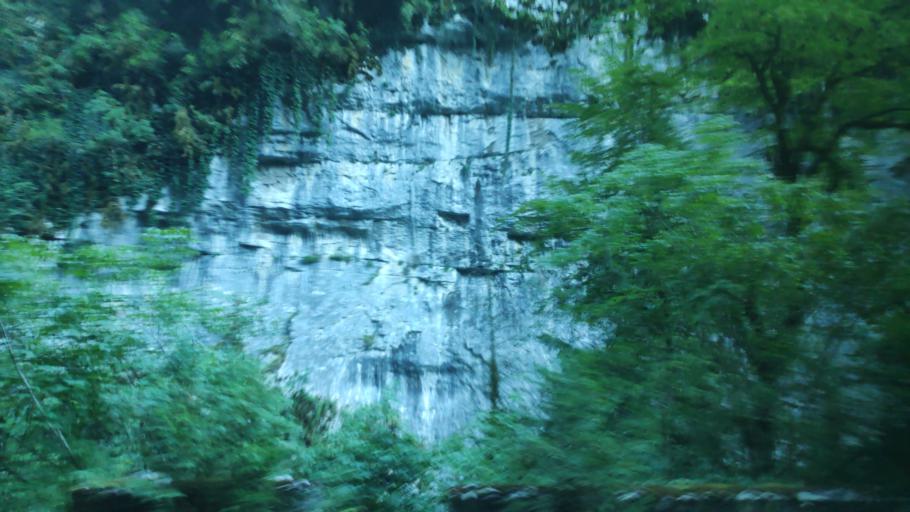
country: GE
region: Abkhazia
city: Gagra
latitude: 43.4365
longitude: 40.5328
